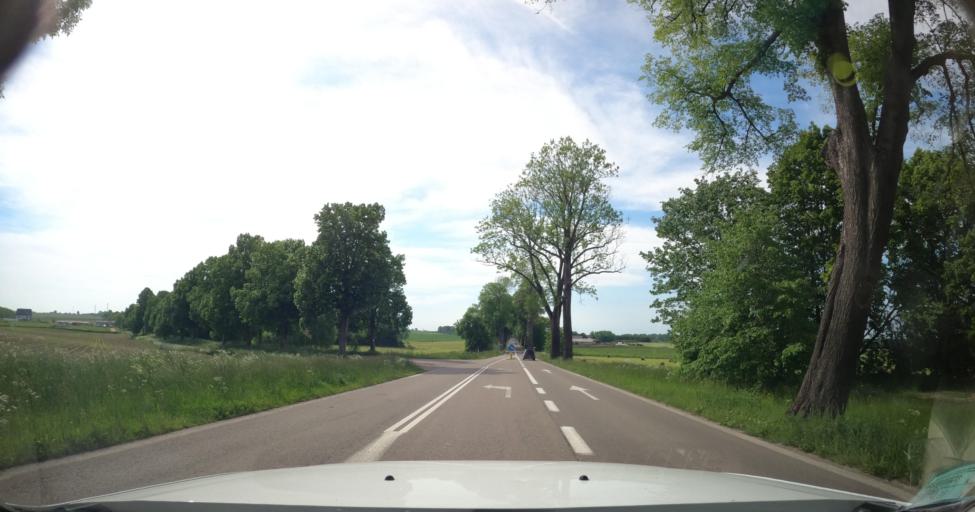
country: PL
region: Warmian-Masurian Voivodeship
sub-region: Powiat lidzbarski
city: Lubomino
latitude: 54.0699
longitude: 20.2269
